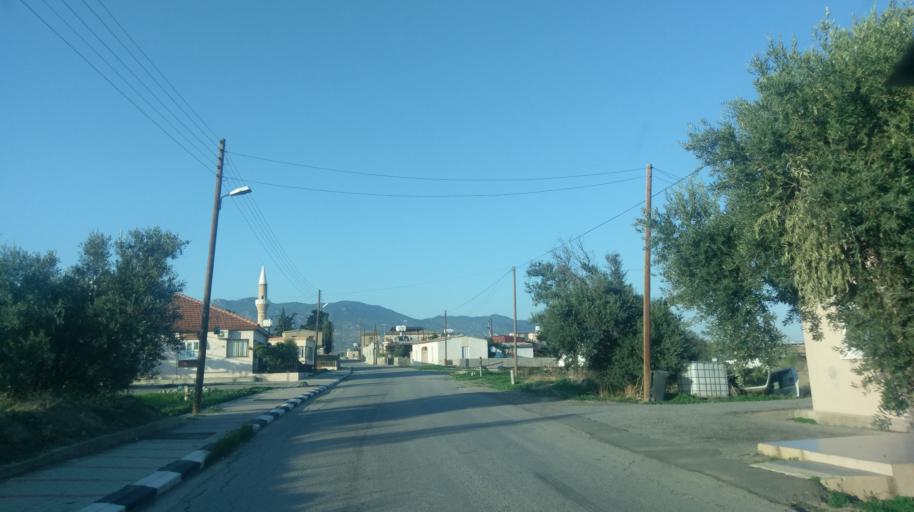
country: CY
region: Larnaka
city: Athienou
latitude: 35.2229
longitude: 33.5559
